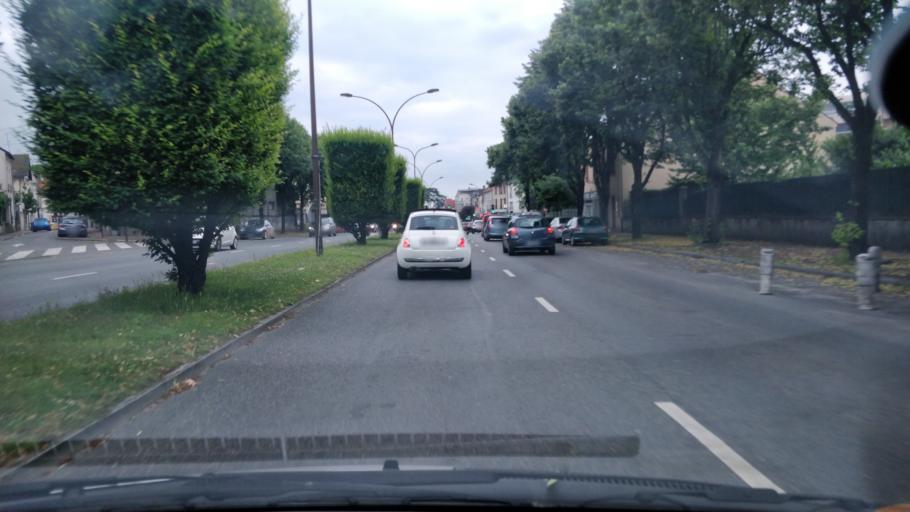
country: FR
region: Ile-de-France
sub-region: Departement de Seine-Saint-Denis
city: Livry-Gargan
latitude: 48.9236
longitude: 2.5460
